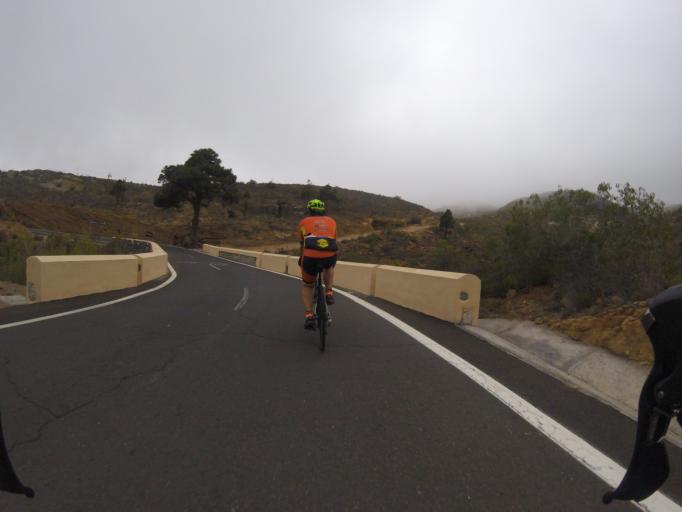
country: ES
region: Canary Islands
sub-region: Provincia de Santa Cruz de Tenerife
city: Lomo de Arico
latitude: 28.2007
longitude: -16.4687
